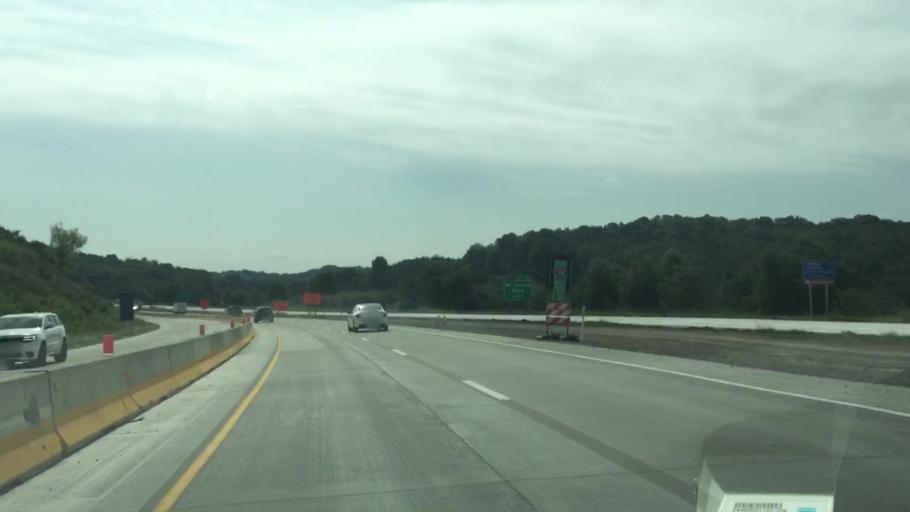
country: US
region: Pennsylvania
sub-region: Allegheny County
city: Enlow
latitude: 40.4901
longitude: -80.2512
